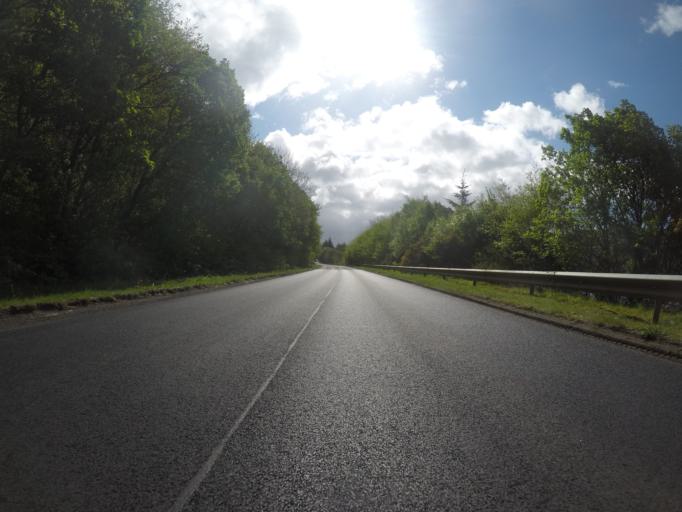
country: GB
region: Scotland
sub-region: Highland
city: Fort William
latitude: 57.2515
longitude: -5.4741
